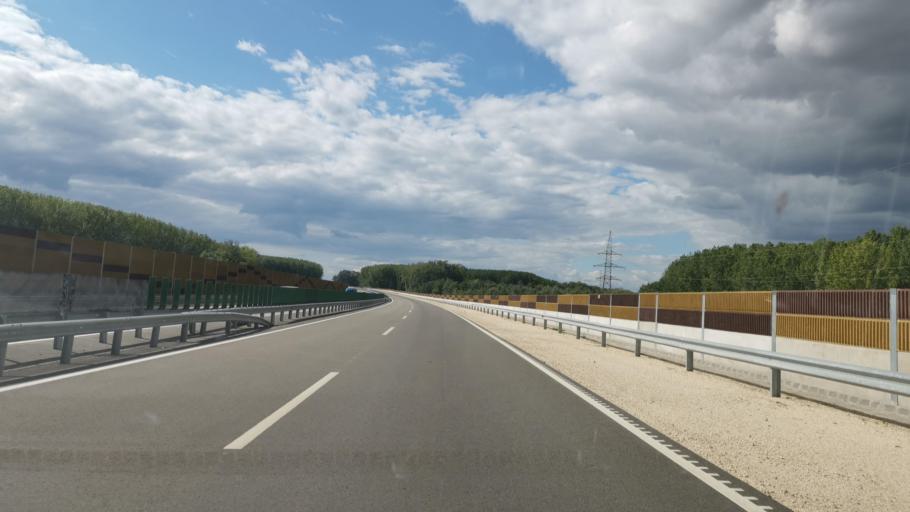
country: HU
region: Jasz-Nagykun-Szolnok
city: Tiszapuspoki
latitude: 47.2086
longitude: 20.3098
